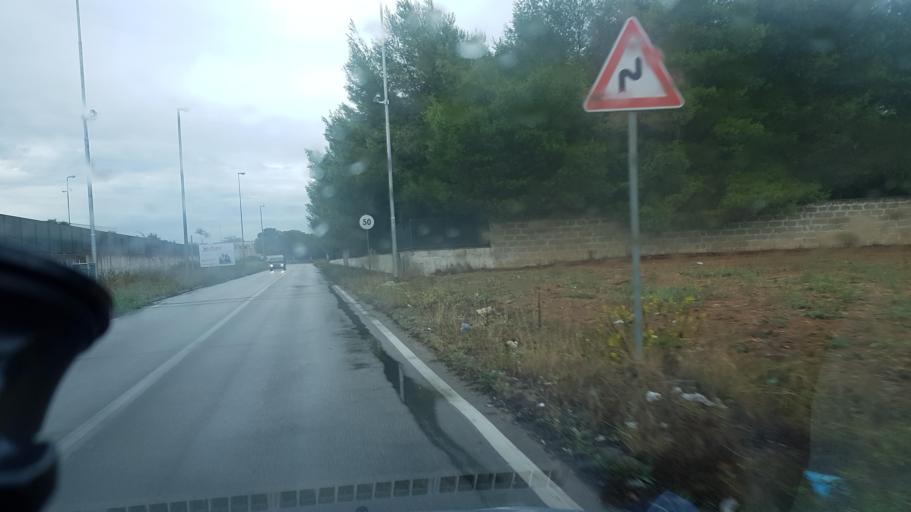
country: IT
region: Apulia
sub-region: Provincia di Lecce
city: Giorgilorio
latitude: 40.3758
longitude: 18.1379
